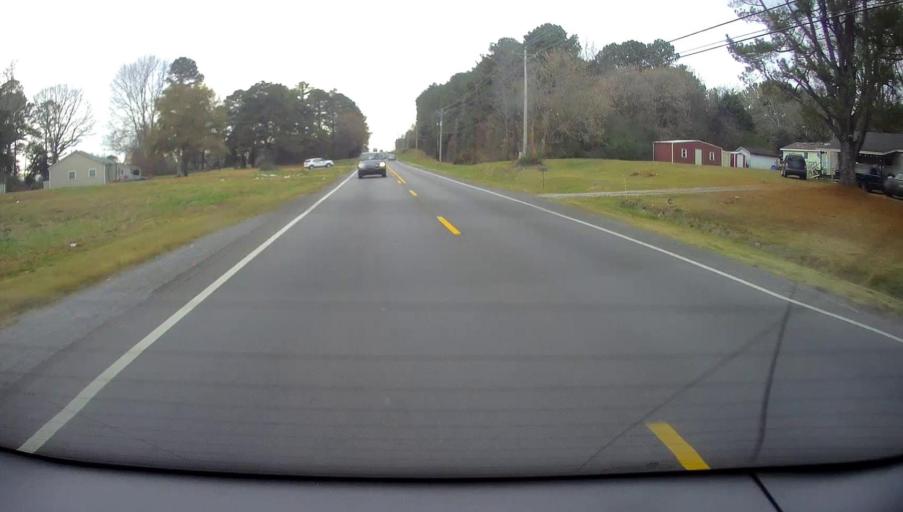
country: US
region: Alabama
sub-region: Morgan County
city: Priceville
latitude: 34.5032
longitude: -86.8608
